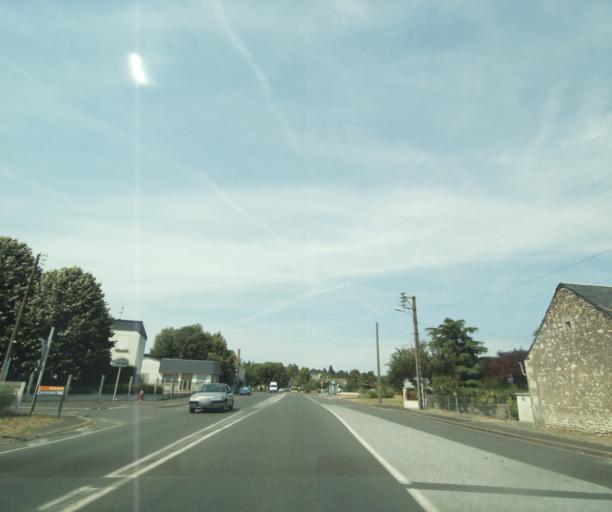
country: FR
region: Centre
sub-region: Departement d'Indre-et-Loire
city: Sainte-Maure-de-Touraine
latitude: 47.1075
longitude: 0.6137
